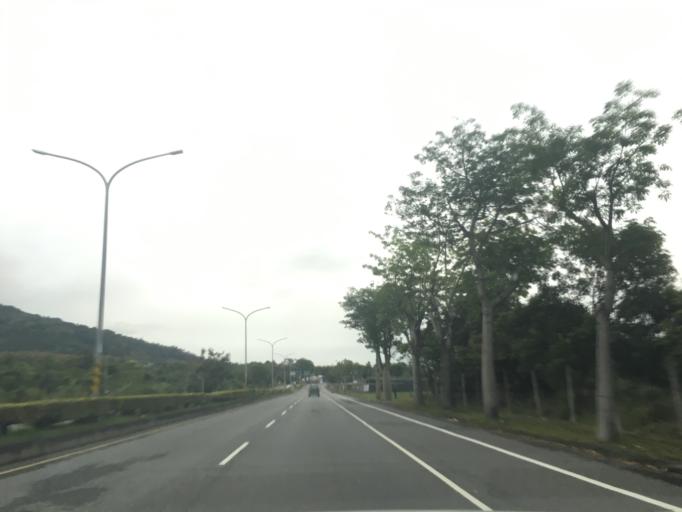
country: TW
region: Taiwan
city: Taitung City
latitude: 22.7100
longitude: 121.0438
